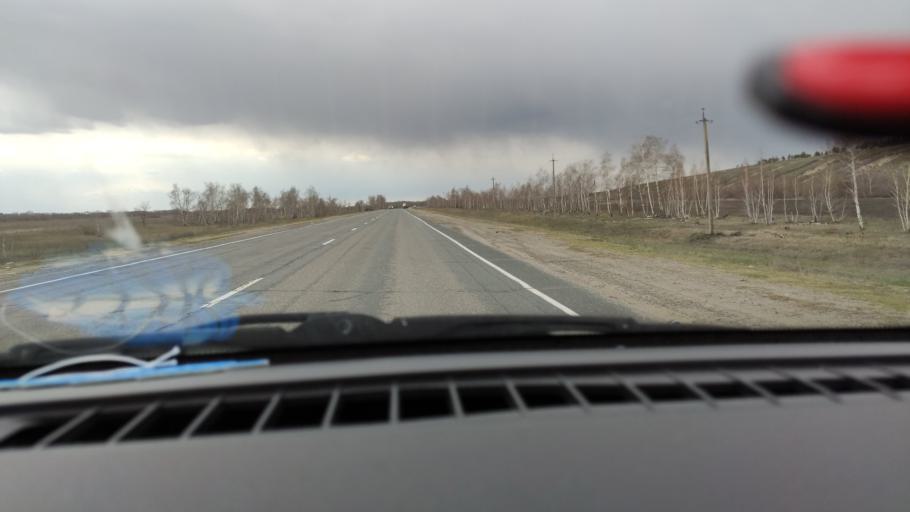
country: RU
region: Saratov
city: Sinodskoye
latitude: 52.0572
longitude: 46.7598
